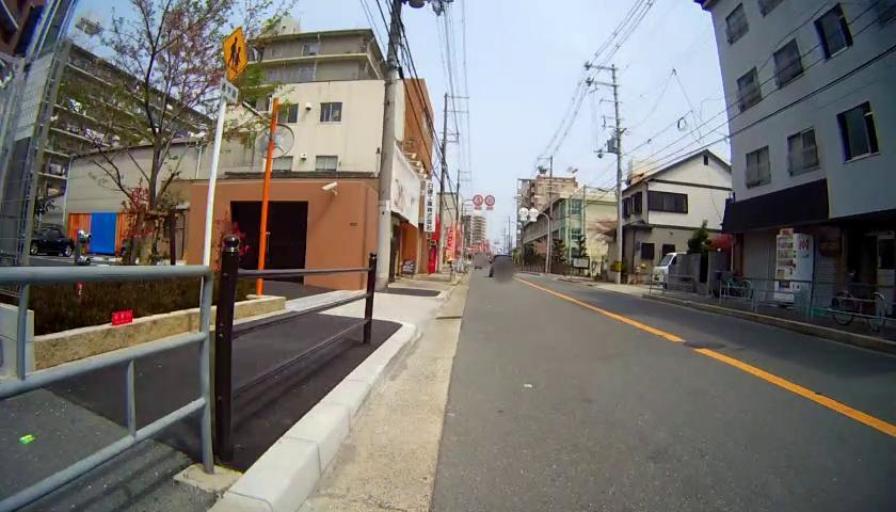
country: JP
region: Osaka
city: Suita
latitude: 34.7549
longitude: 135.5383
